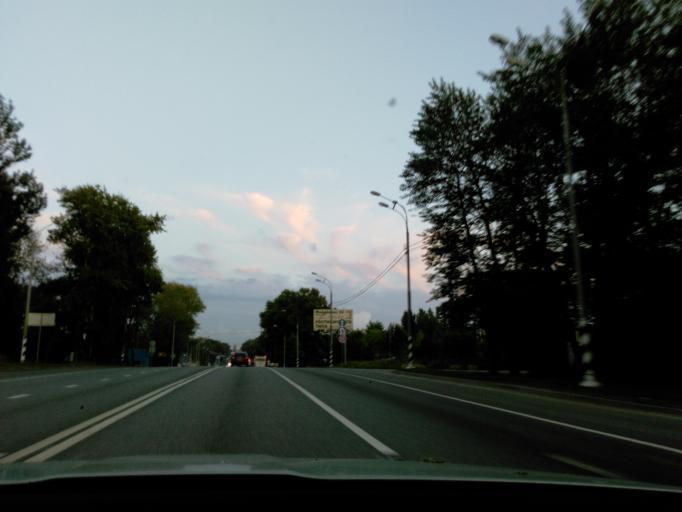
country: RU
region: Moskovskaya
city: Klin
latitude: 56.3495
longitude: 36.7050
